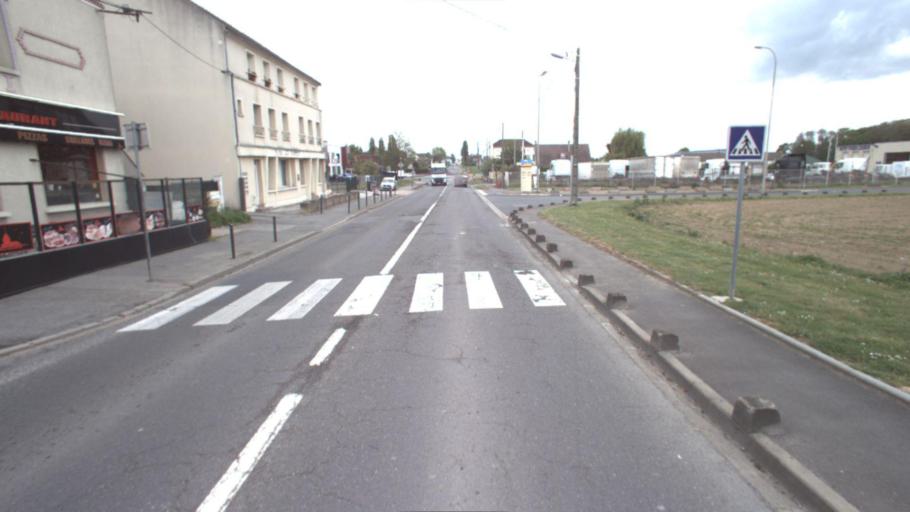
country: FR
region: Picardie
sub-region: Departement de l'Oise
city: Lagny-le-Sec
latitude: 49.0951
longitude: 2.7446
